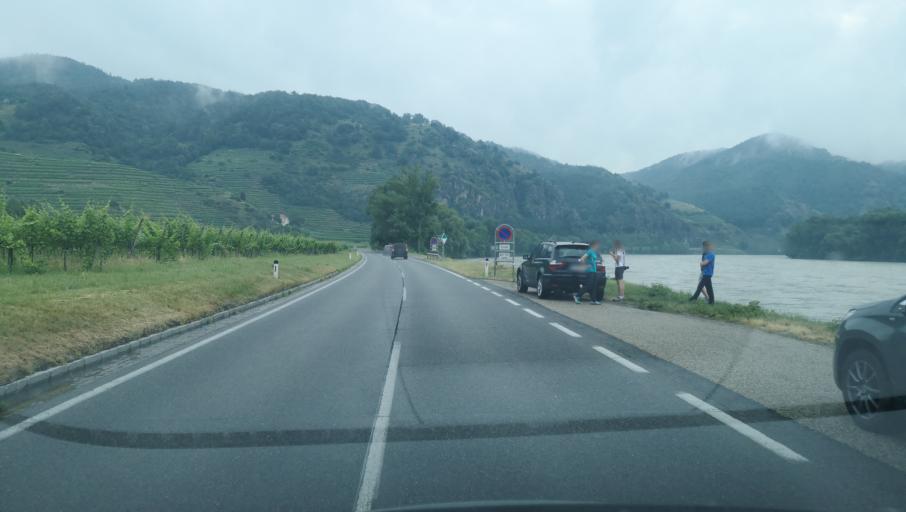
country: AT
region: Lower Austria
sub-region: Politischer Bezirk Krems
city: Durnstein
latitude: 48.4083
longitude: 15.4912
